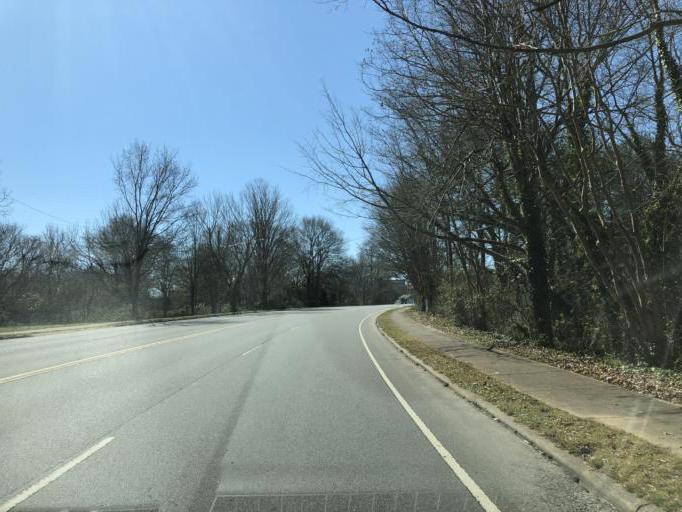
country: US
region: North Carolina
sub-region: Cleveland County
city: Shelby
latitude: 35.2961
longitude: -81.5354
